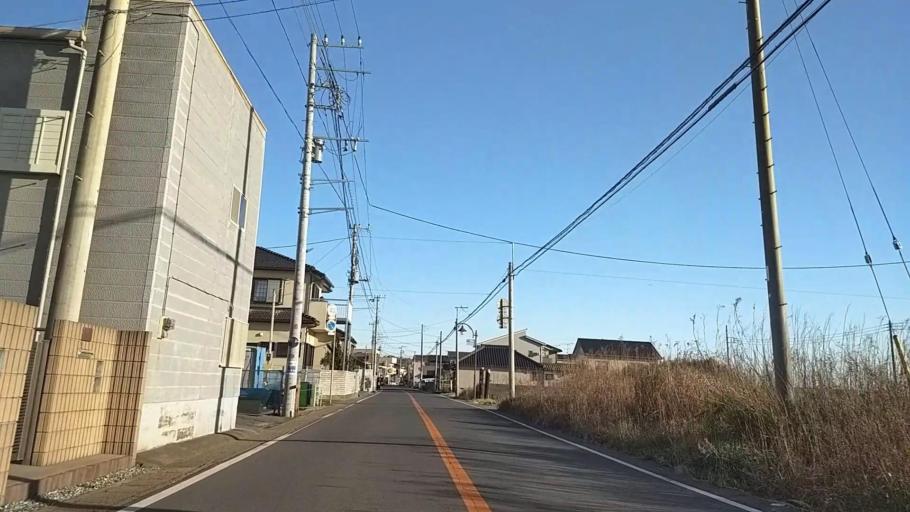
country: JP
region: Chiba
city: Asahi
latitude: 35.7014
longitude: 140.7193
